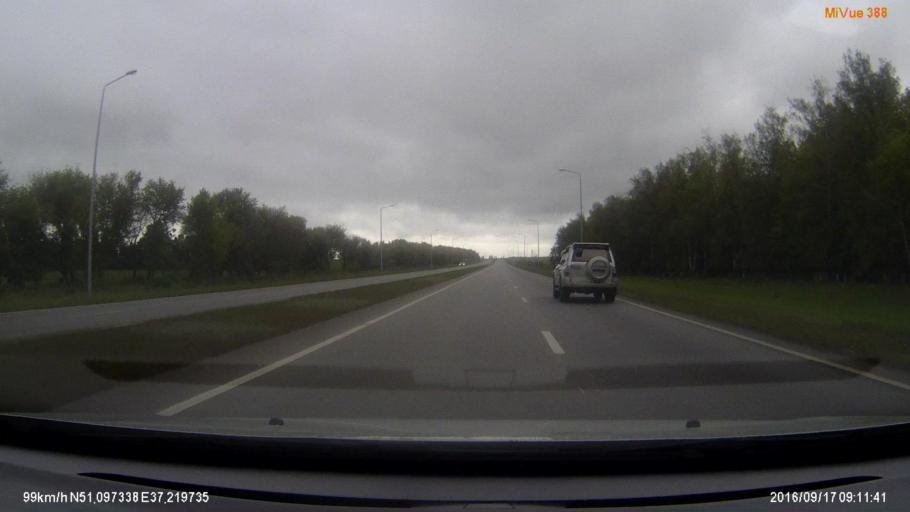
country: RU
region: Belgorod
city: Skorodnoye
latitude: 51.0970
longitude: 37.2196
